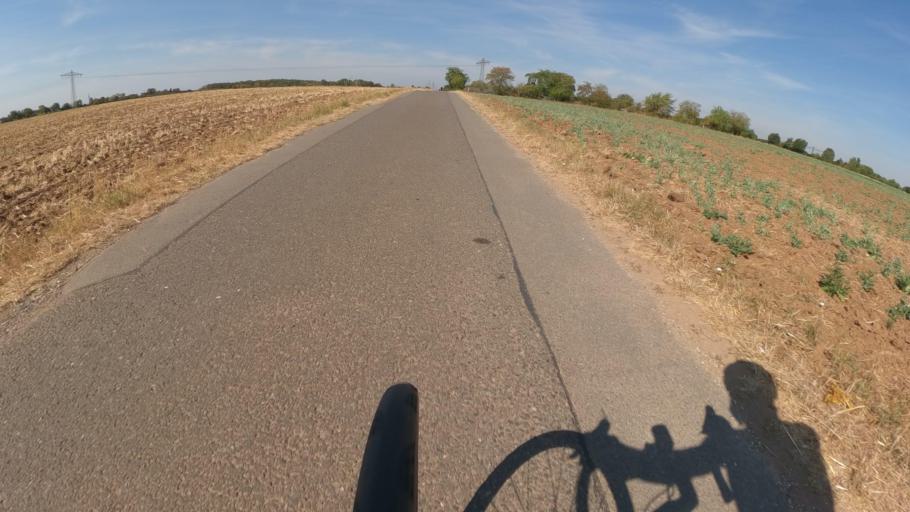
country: DE
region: Baden-Wuerttemberg
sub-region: Karlsruhe Region
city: Eppelheim
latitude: 49.3856
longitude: 8.6312
